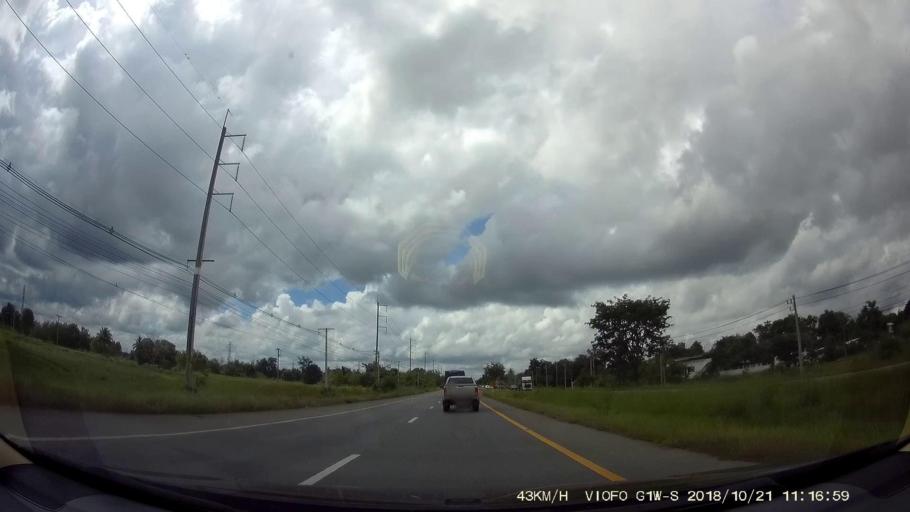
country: TH
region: Chaiyaphum
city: Chaiyaphum
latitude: 15.8806
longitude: 102.0986
